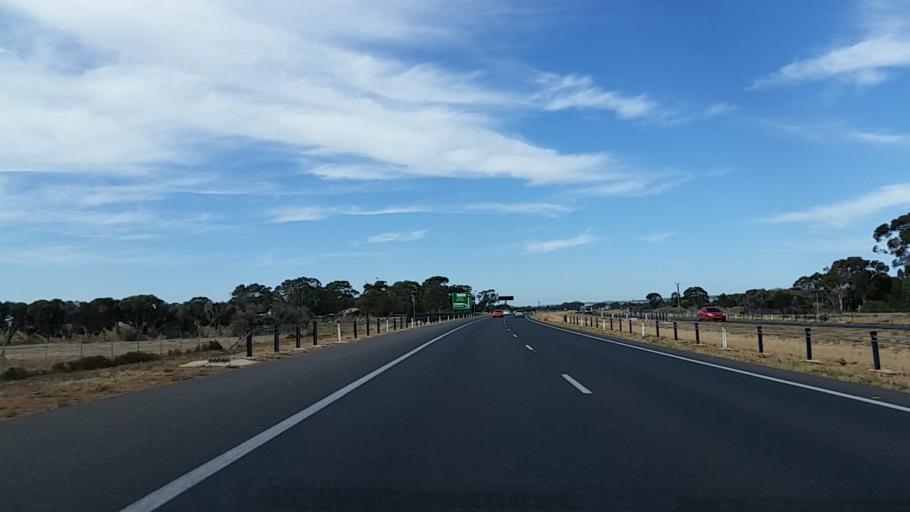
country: AU
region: South Australia
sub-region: Playford
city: Virginia
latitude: -34.6814
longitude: 138.6061
